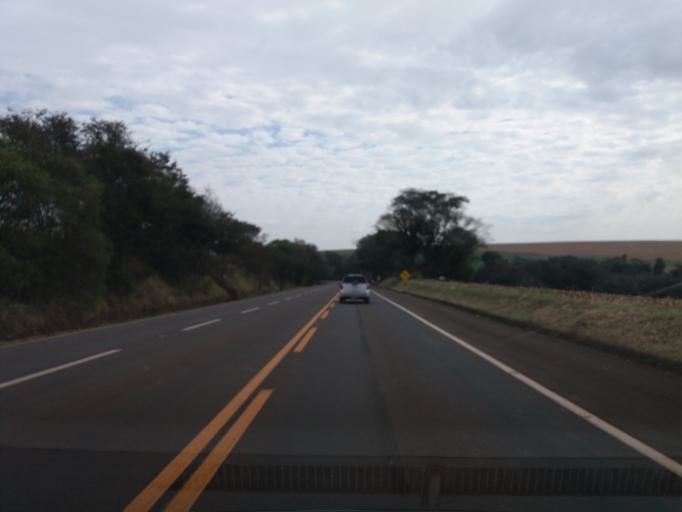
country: BR
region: Parana
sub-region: Campo Mourao
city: Campo Mourao
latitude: -24.3196
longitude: -52.6350
